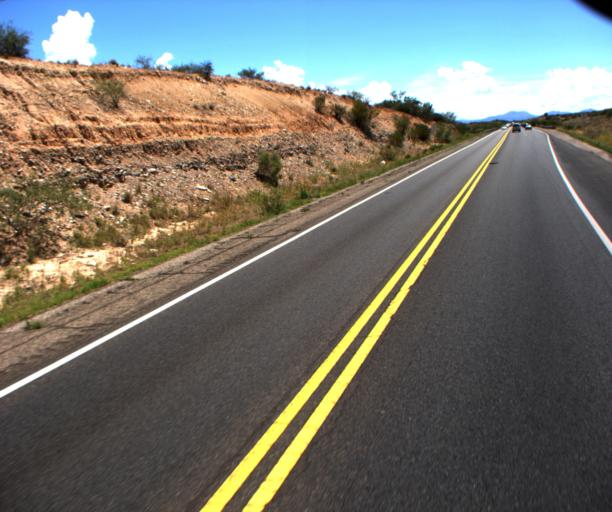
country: US
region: Arizona
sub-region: Yavapai County
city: Cornville
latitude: 34.6355
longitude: -111.9409
